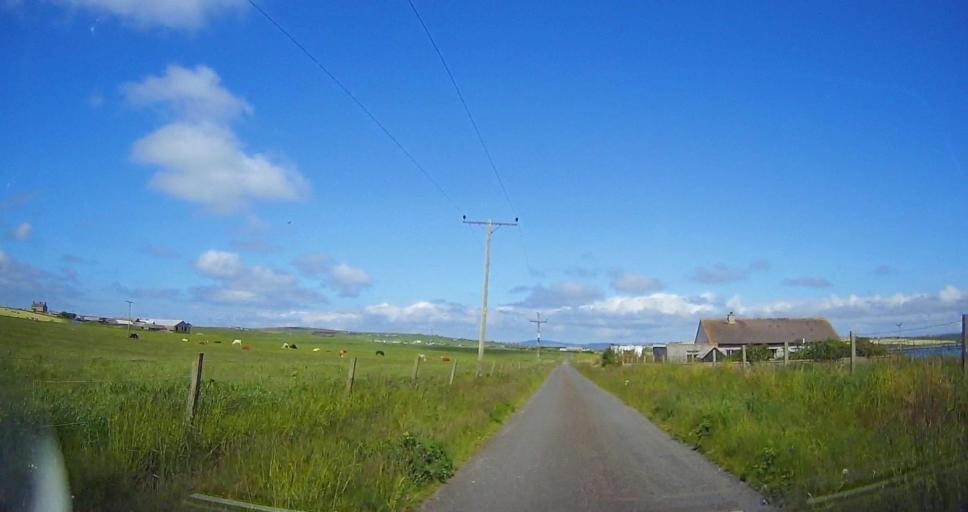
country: GB
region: Scotland
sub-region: Orkney Islands
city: Kirkwall
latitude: 58.8310
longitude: -2.8981
